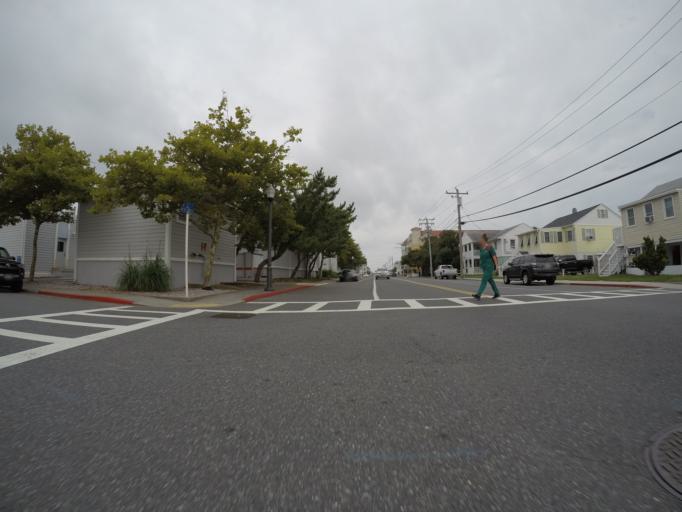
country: US
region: Maryland
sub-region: Worcester County
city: Ocean City
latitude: 38.3457
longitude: -75.0812
